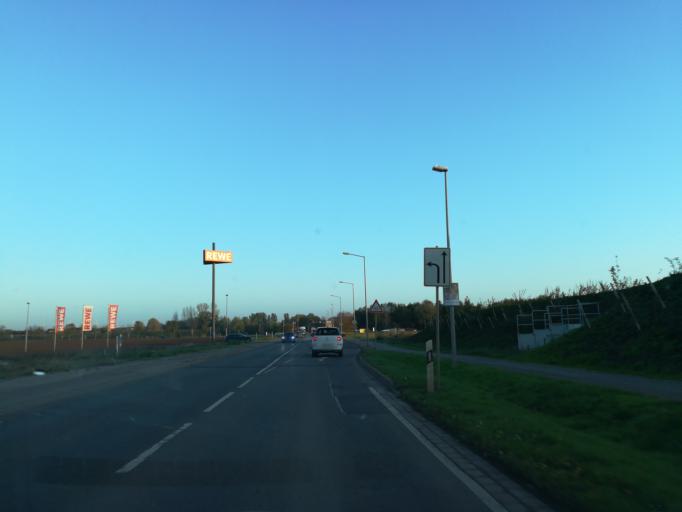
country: DE
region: Saxony-Anhalt
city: Diesdorf
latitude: 52.1385
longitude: 11.5725
